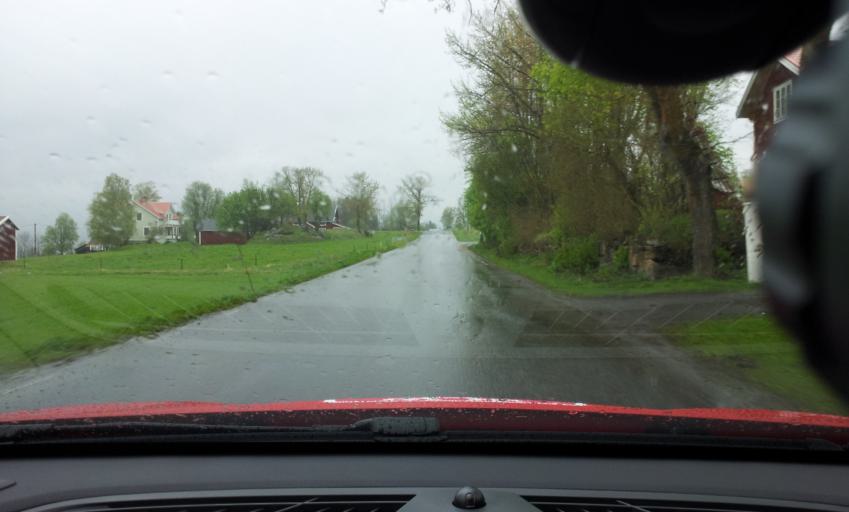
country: SE
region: Jaemtland
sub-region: Bergs Kommun
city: Hoverberg
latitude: 62.9558
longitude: 14.4905
